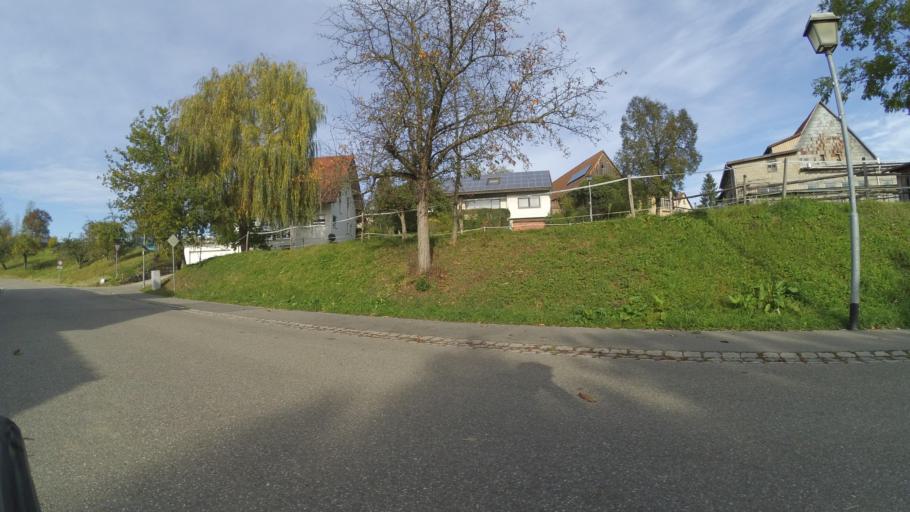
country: DE
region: Baden-Wuerttemberg
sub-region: Regierungsbezirk Stuttgart
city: Ohringen
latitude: 49.2043
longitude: 9.5370
